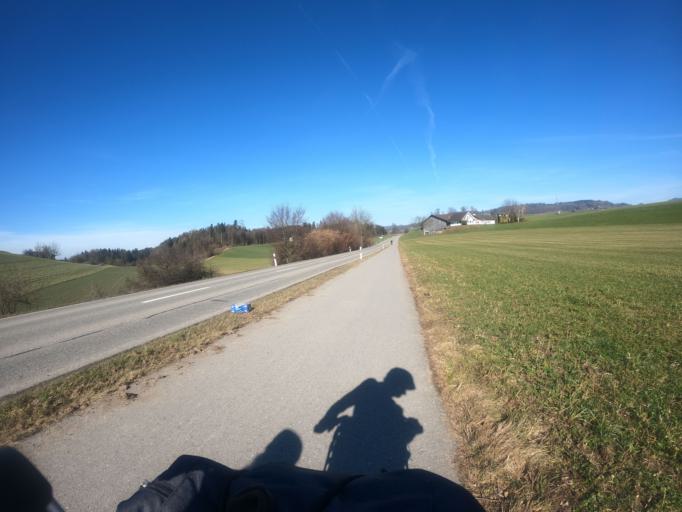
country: CH
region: Zurich
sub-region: Bezirk Affoltern
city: Mettmenstetten
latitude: 47.2353
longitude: 8.4496
